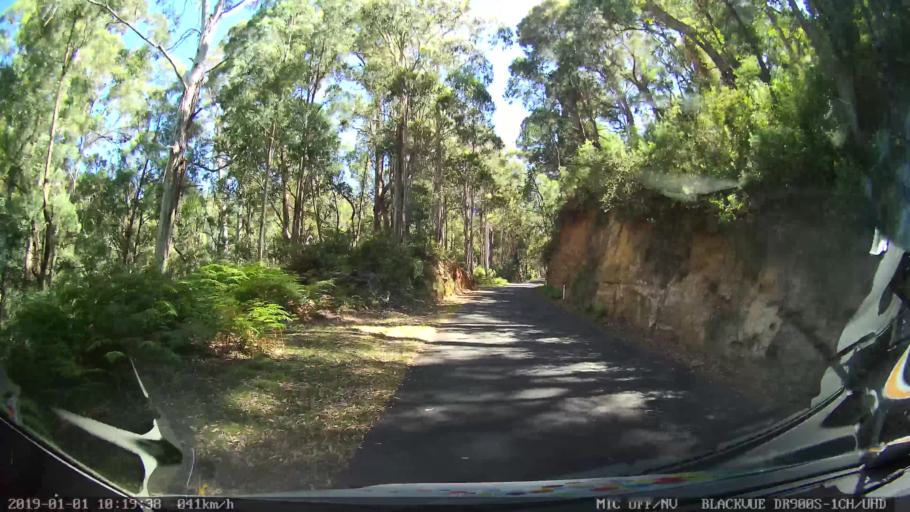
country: AU
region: New South Wales
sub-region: Snowy River
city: Jindabyne
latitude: -36.0832
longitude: 148.1859
